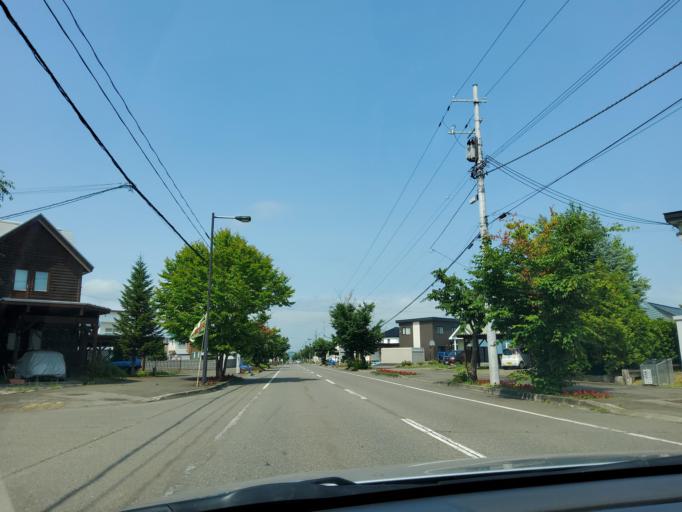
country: JP
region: Hokkaido
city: Obihiro
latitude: 42.8987
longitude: 143.0460
